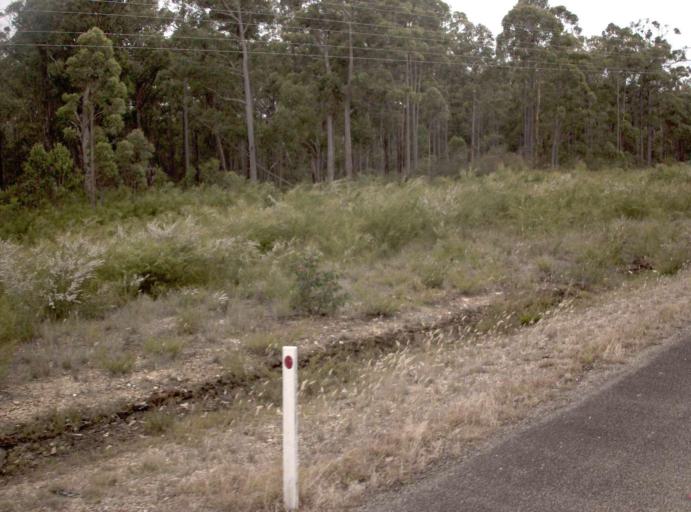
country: AU
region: Victoria
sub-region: East Gippsland
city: Lakes Entrance
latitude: -37.7158
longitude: 147.9712
